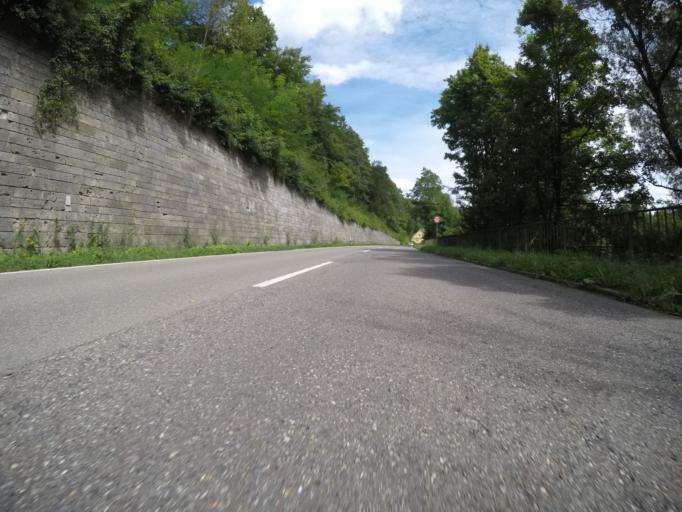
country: DE
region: Baden-Wuerttemberg
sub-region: Karlsruhe Region
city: Horb am Neckar
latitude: 48.4545
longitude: 8.7438
